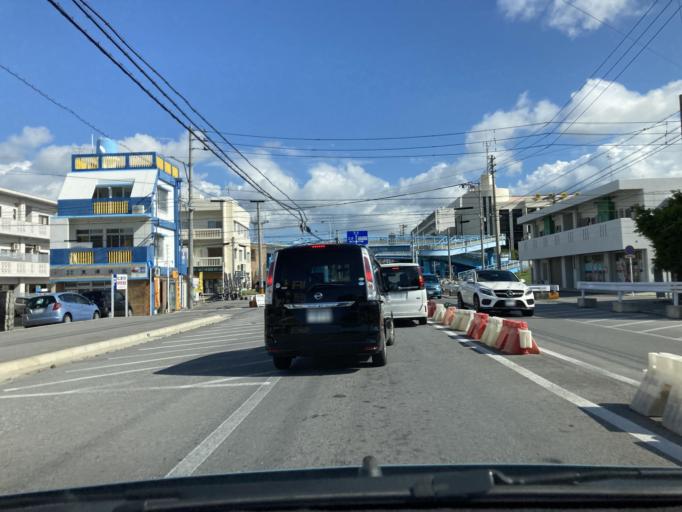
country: JP
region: Okinawa
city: Naha-shi
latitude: 26.2084
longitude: 127.6904
